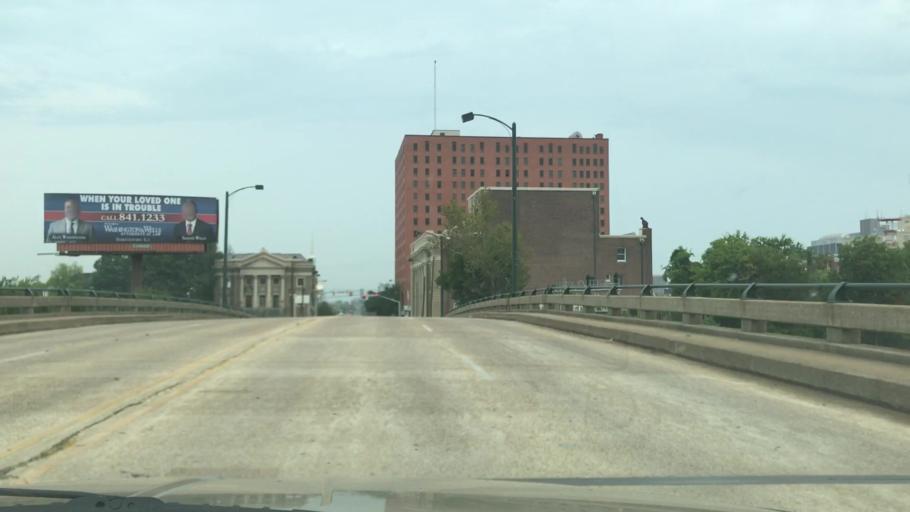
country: US
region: Louisiana
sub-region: Caddo Parish
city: Shreveport
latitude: 32.5070
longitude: -93.7489
